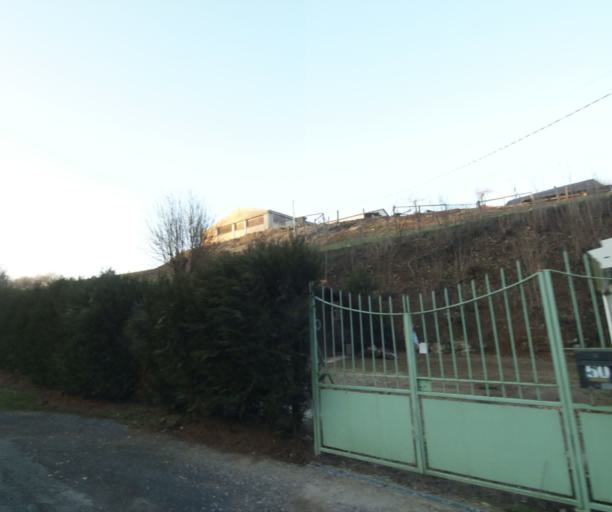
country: FR
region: Champagne-Ardenne
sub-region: Departement de la Haute-Marne
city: Bienville
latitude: 48.6114
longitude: 5.0654
